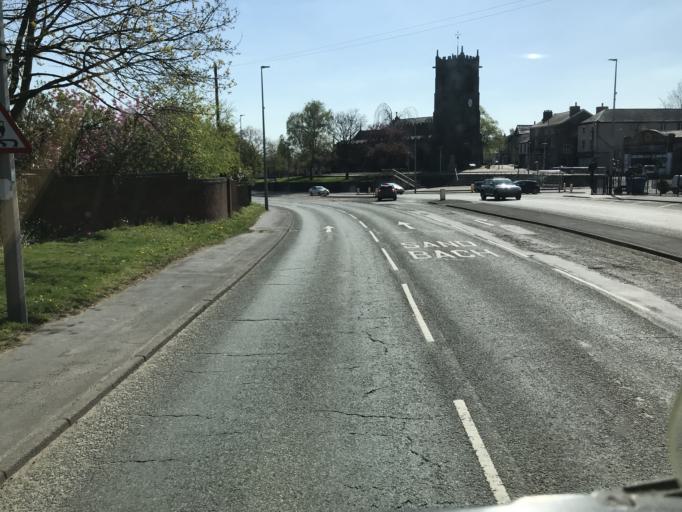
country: GB
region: England
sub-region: Cheshire East
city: Middlewich
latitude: 53.1934
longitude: -2.4464
